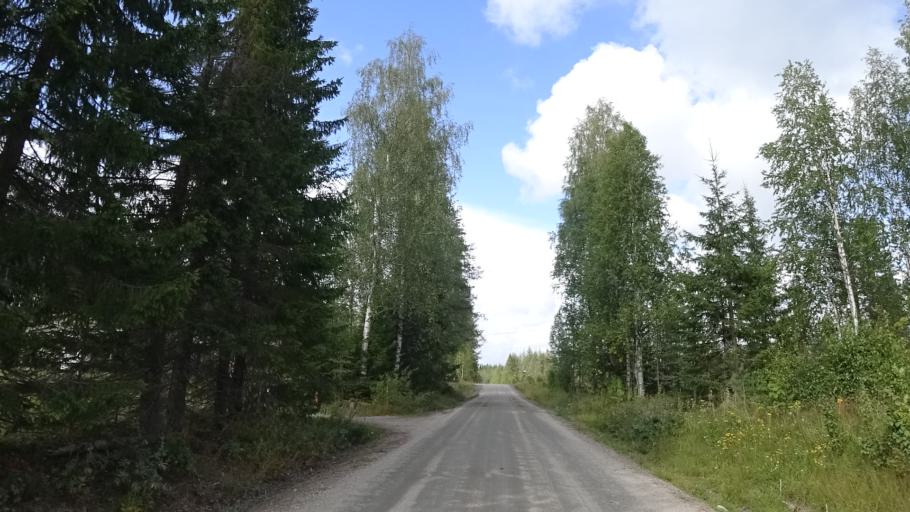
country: FI
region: North Karelia
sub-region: Pielisen Karjala
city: Lieksa
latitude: 63.5874
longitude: 30.1348
